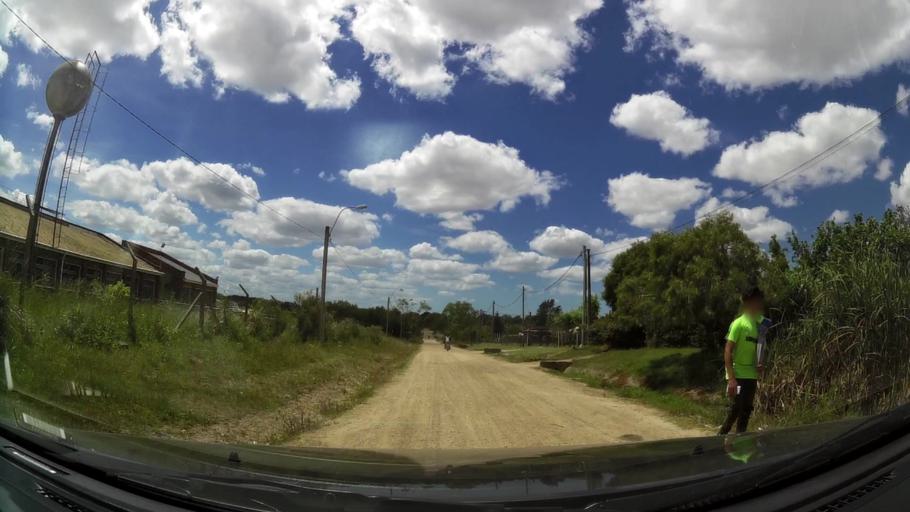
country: UY
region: Canelones
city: Colonia Nicolich
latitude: -34.7913
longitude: -55.9980
